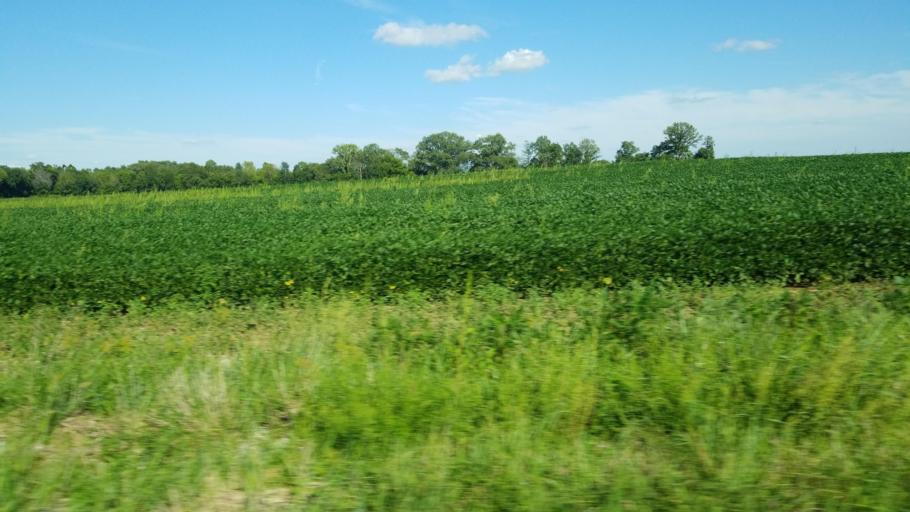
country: US
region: Illinois
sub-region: Saline County
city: Harrisburg
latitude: 37.8139
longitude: -88.5673
